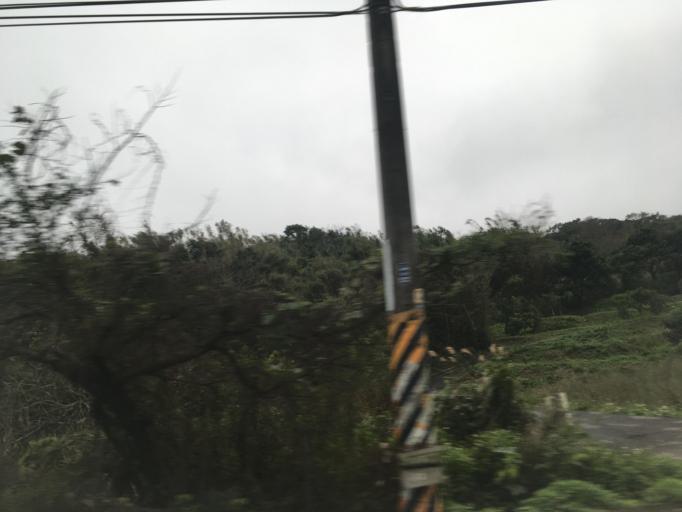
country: TW
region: Taiwan
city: Fengyuan
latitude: 24.4137
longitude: 120.7340
